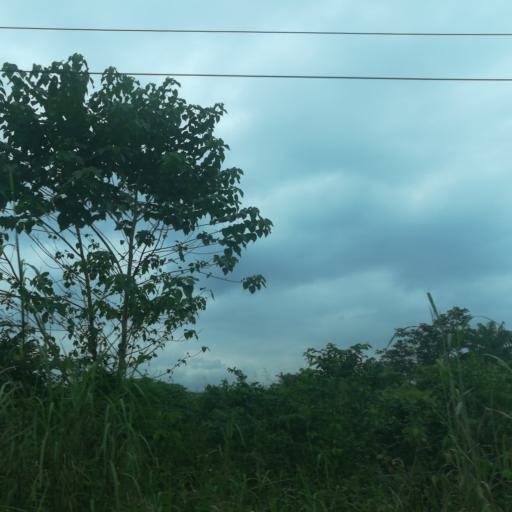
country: NG
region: Lagos
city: Ejirin
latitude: 6.6541
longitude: 3.8236
